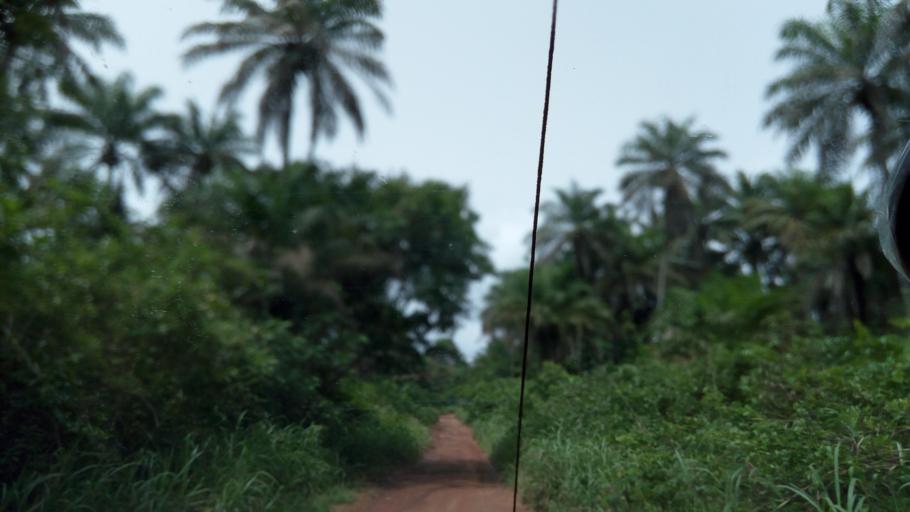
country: SL
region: Northern Province
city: Kambia
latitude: 9.1039
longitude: -12.9872
